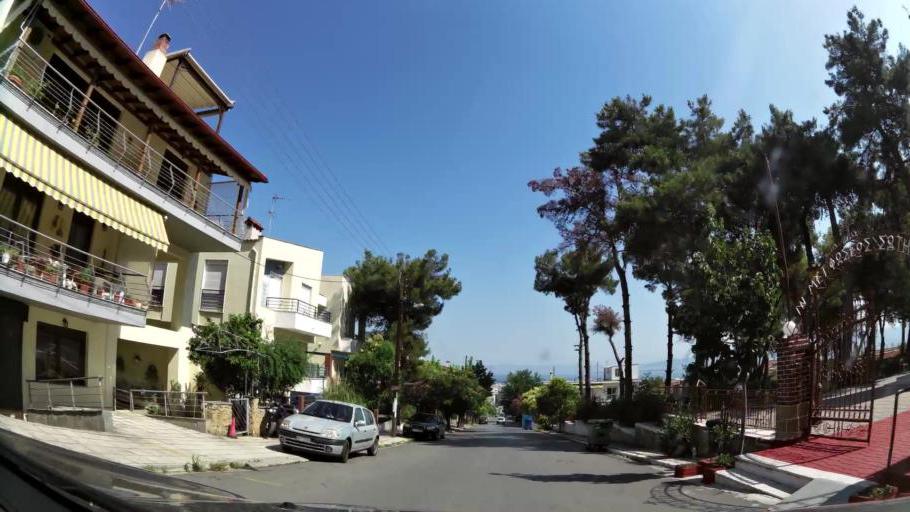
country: GR
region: Central Macedonia
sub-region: Nomos Thessalonikis
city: Peraia
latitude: 40.4985
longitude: 22.9262
